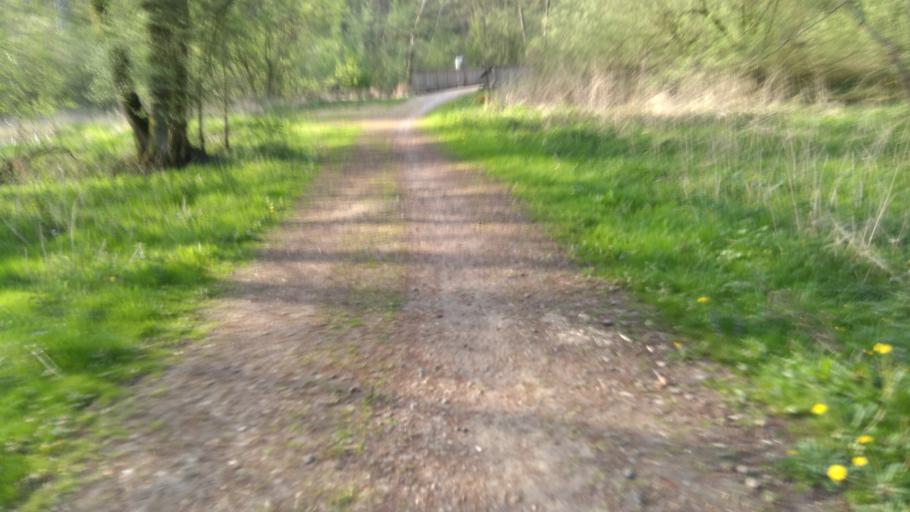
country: DE
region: Lower Saxony
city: Buxtehude
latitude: 53.4392
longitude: 9.6740
